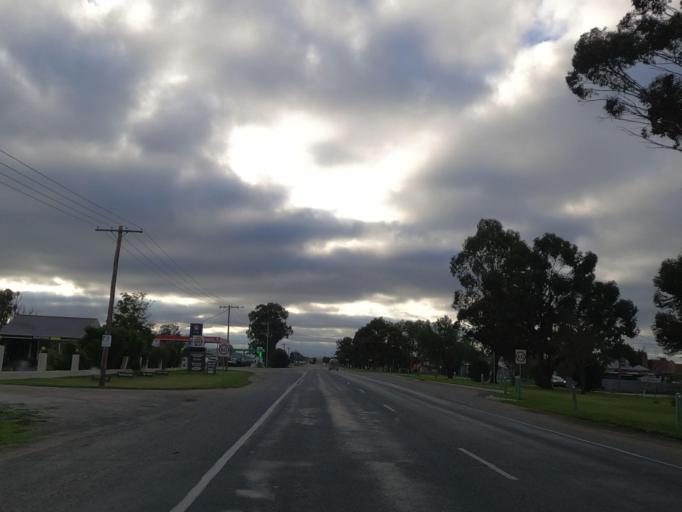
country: AU
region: Victoria
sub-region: Swan Hill
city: Swan Hill
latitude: -35.7407
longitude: 143.9198
